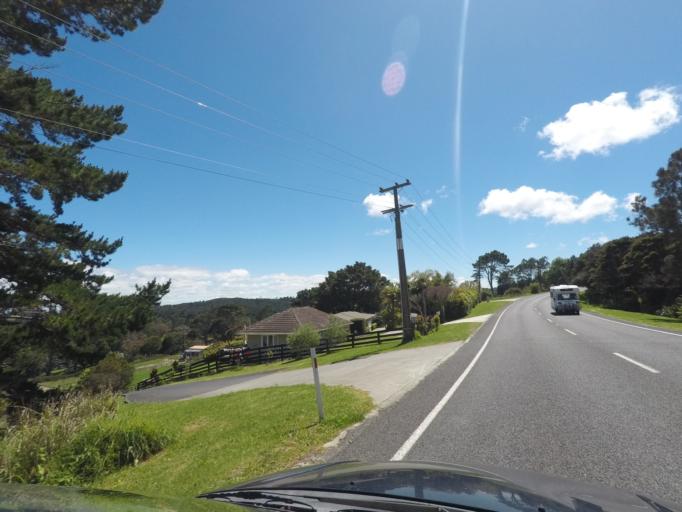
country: NZ
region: Auckland
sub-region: Auckland
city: Rothesay Bay
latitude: -36.7588
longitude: 174.6601
